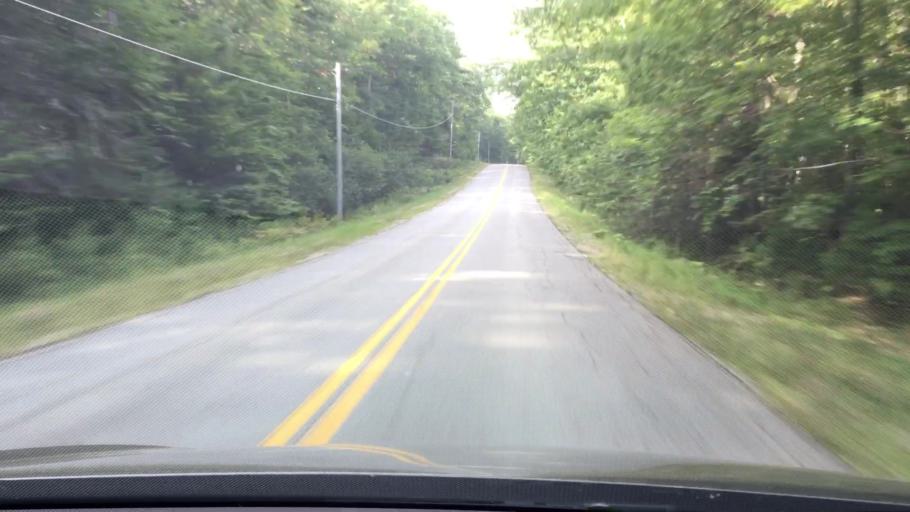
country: US
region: Maine
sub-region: Hancock County
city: Orland
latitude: 44.5270
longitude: -68.7637
